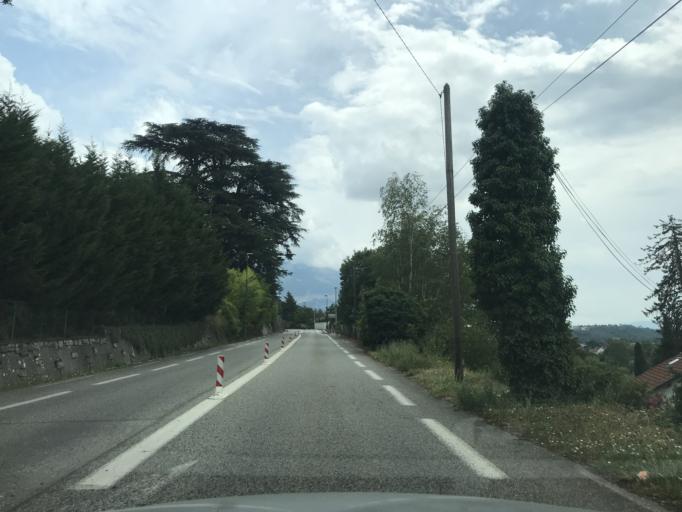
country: FR
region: Rhone-Alpes
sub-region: Departement de la Savoie
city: Brison-Saint-Innocent
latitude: 45.7146
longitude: 5.8900
